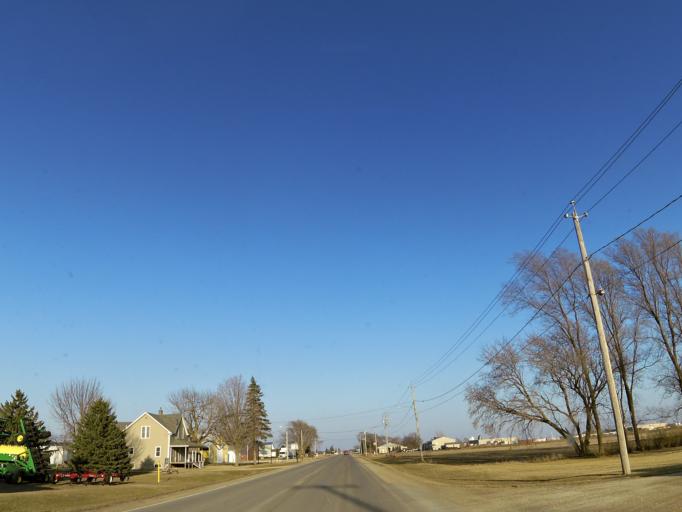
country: US
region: Iowa
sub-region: Worth County
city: Northwood
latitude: 43.4440
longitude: -93.2067
